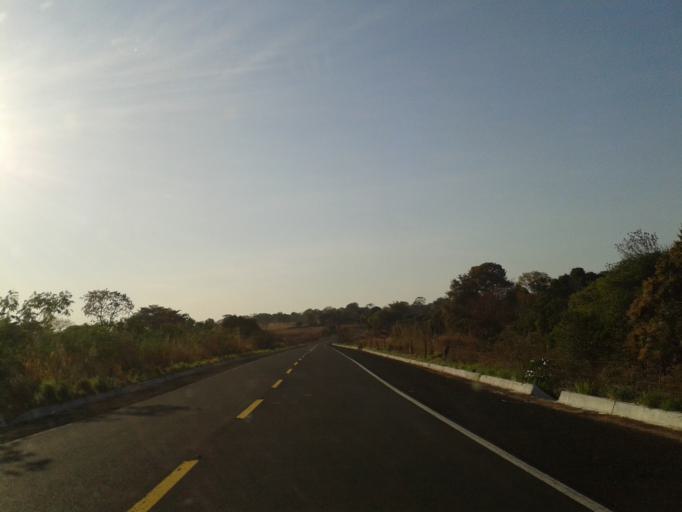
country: BR
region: Minas Gerais
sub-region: Santa Vitoria
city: Santa Vitoria
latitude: -19.1714
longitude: -50.0529
